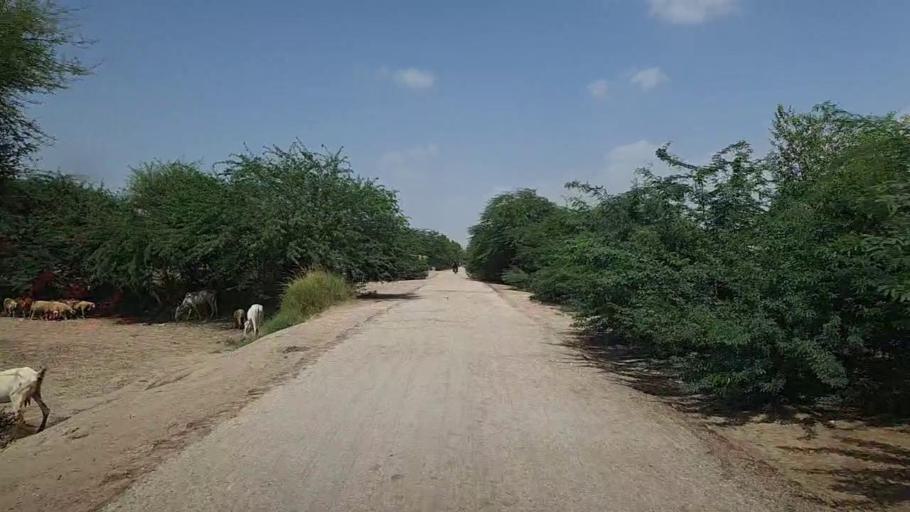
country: PK
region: Sindh
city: Pad Idan
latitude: 26.8056
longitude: 68.3803
